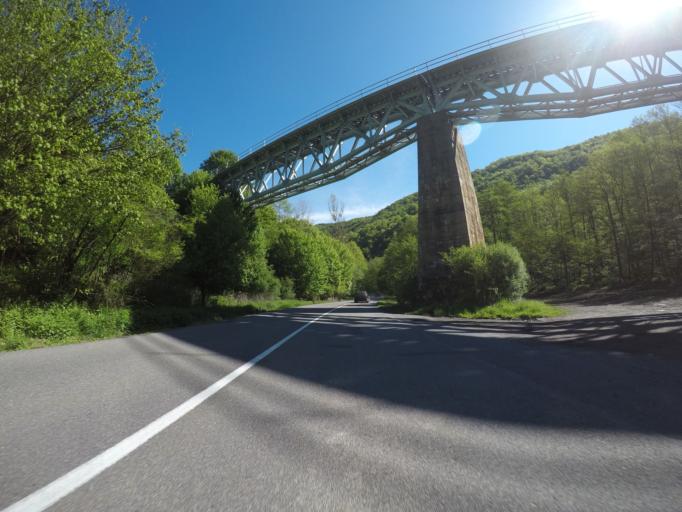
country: SK
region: Banskobystricky
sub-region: Okres Banska Bystrica
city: Banska Stiavnica
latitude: 48.5279
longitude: 19.0049
